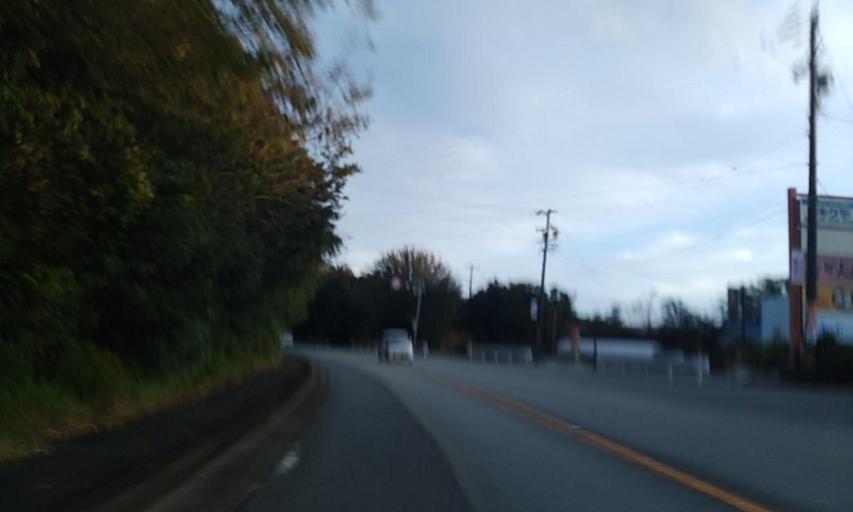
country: JP
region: Mie
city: Toba
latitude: 34.3213
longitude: 136.8495
